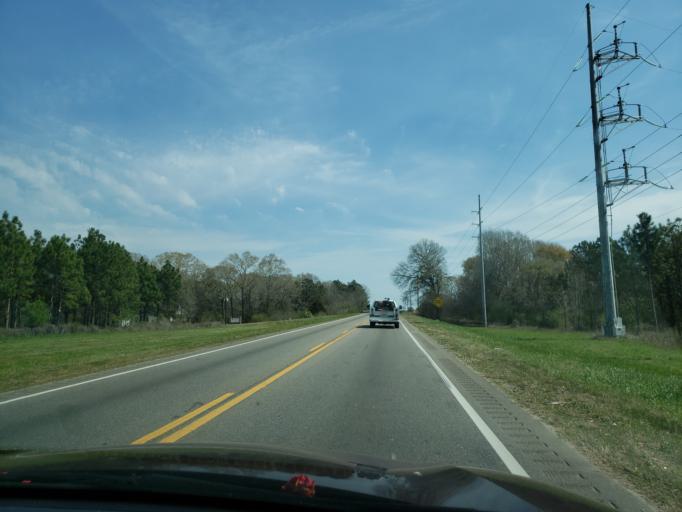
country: US
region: Alabama
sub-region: Autauga County
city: Prattville
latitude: 32.4369
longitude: -86.4429
